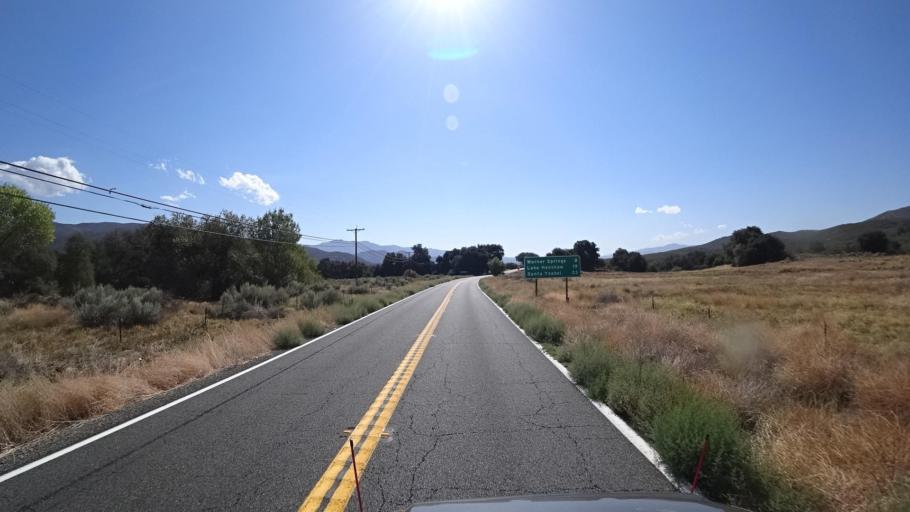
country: US
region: California
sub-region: Riverside County
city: Aguanga
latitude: 33.3419
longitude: -116.7236
